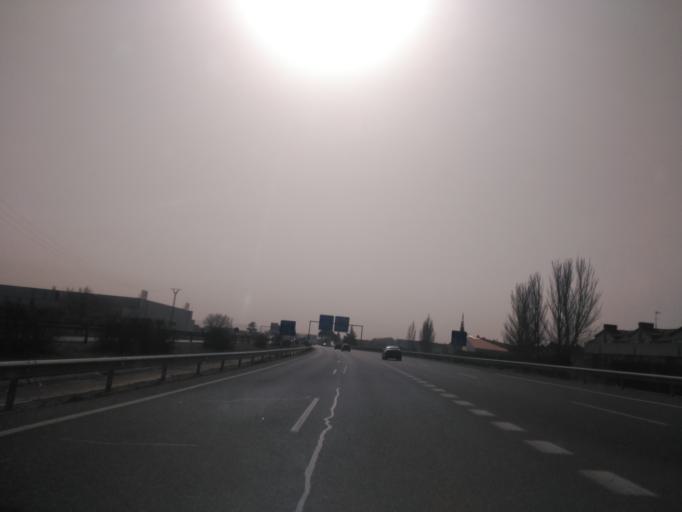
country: ES
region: Castille and Leon
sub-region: Provincia de Palencia
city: Villamuriel de Cerrato
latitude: 41.9482
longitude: -4.5047
